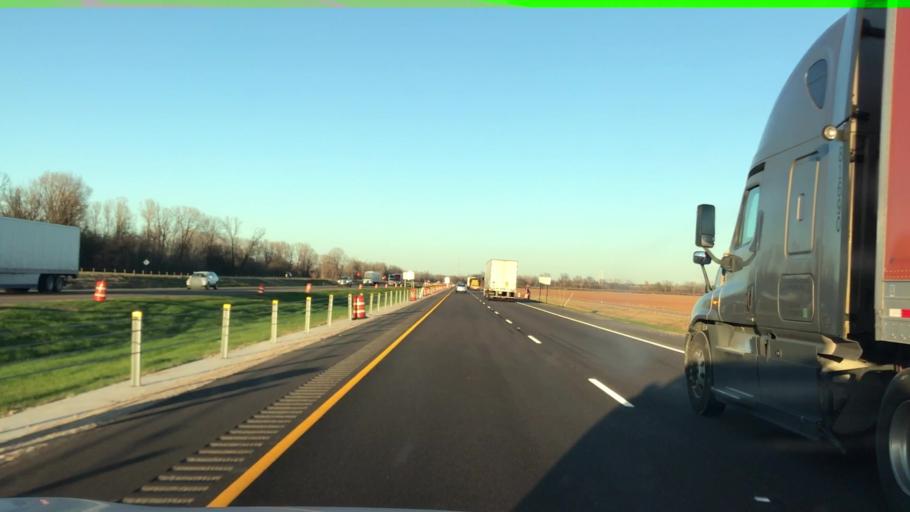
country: US
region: Arkansas
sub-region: Miller County
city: Texarkana
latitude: 33.5910
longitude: -93.8341
